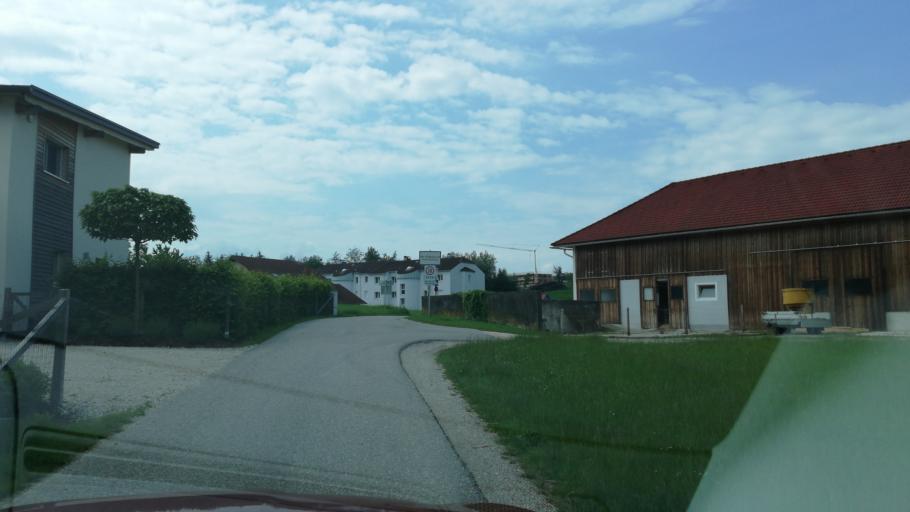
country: AT
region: Upper Austria
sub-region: Politischer Bezirk Steyr-Land
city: Bad Hall
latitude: 48.0475
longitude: 14.2086
